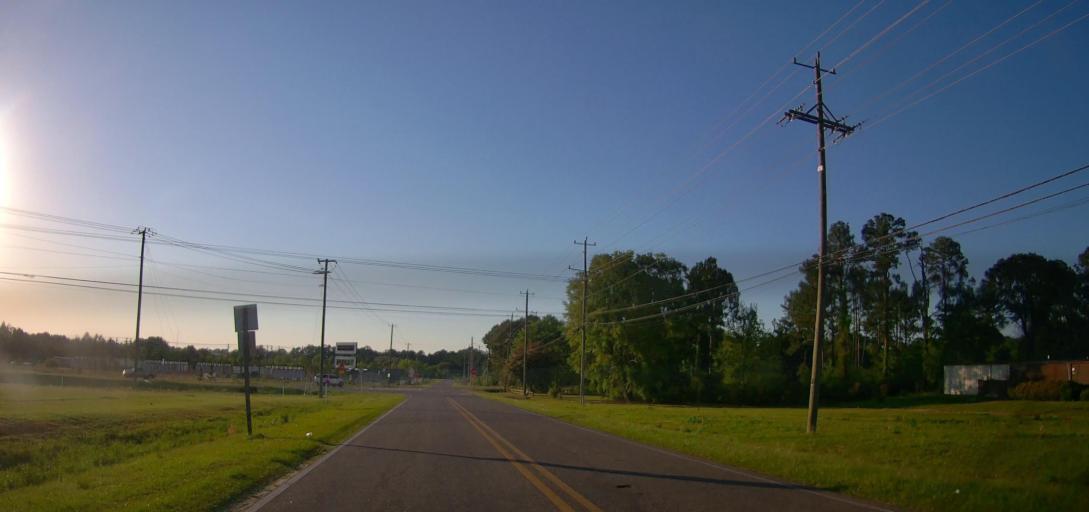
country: US
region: Georgia
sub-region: Ben Hill County
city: Fitzgerald
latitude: 31.6972
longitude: -83.2384
